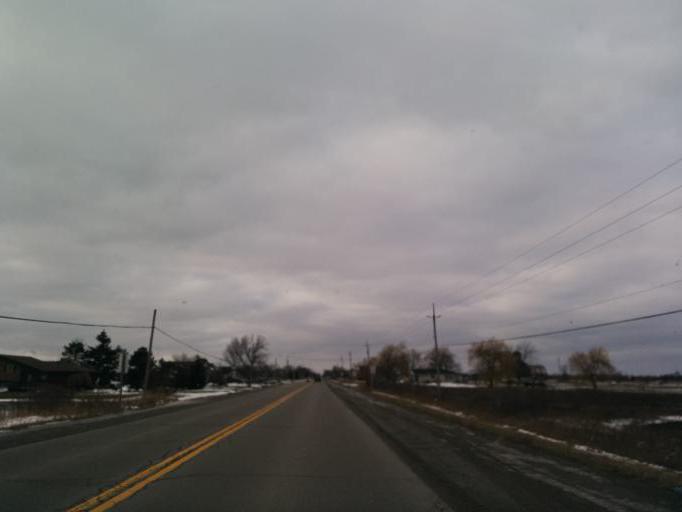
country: CA
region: Ontario
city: Ancaster
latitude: 42.9548
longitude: -80.0316
